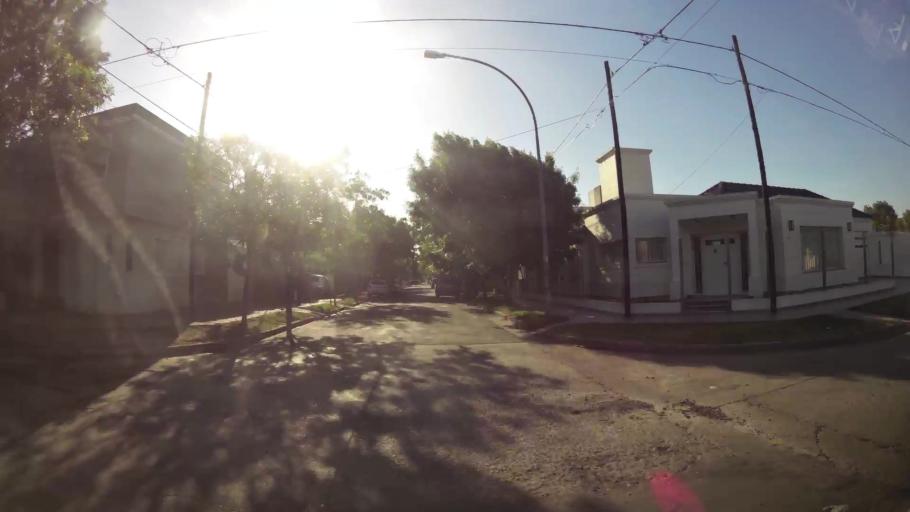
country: AR
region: Cordoba
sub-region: Departamento de Capital
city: Cordoba
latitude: -31.3575
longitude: -64.2128
